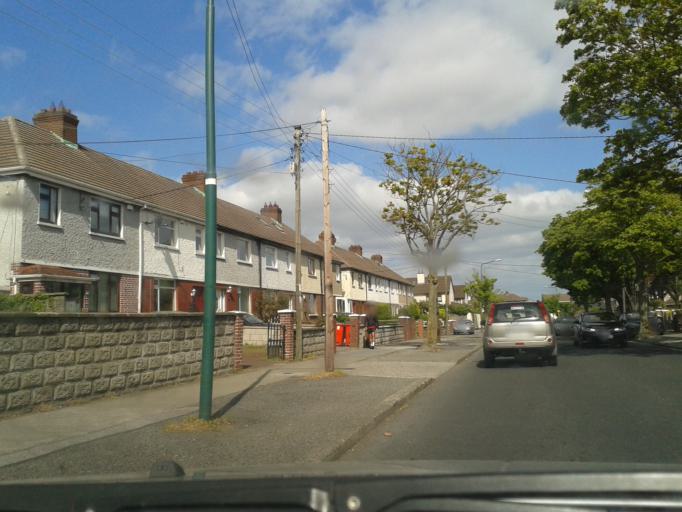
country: IE
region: Leinster
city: Beaumont
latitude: 53.3897
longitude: -6.2490
